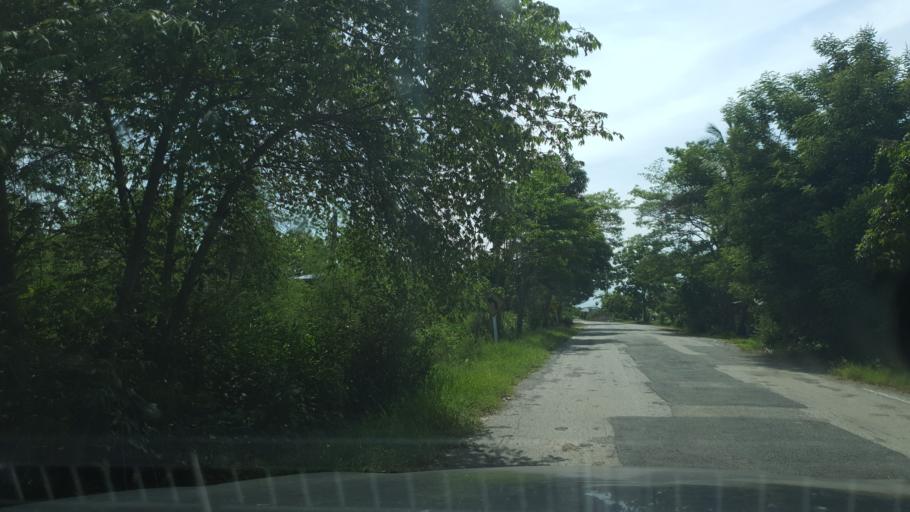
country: TH
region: Sukhothai
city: Si Samrong
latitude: 17.1945
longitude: 99.7363
